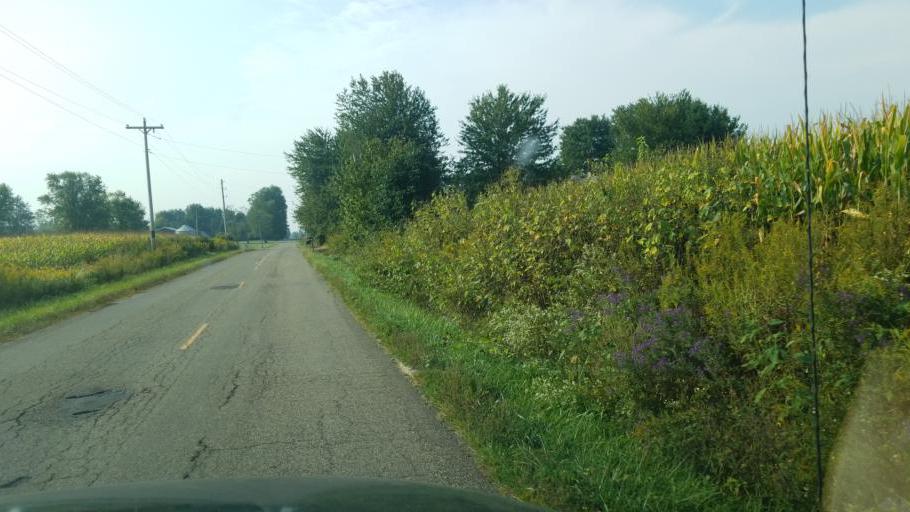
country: US
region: Ohio
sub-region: Knox County
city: Centerburg
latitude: 40.2956
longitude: -82.6013
